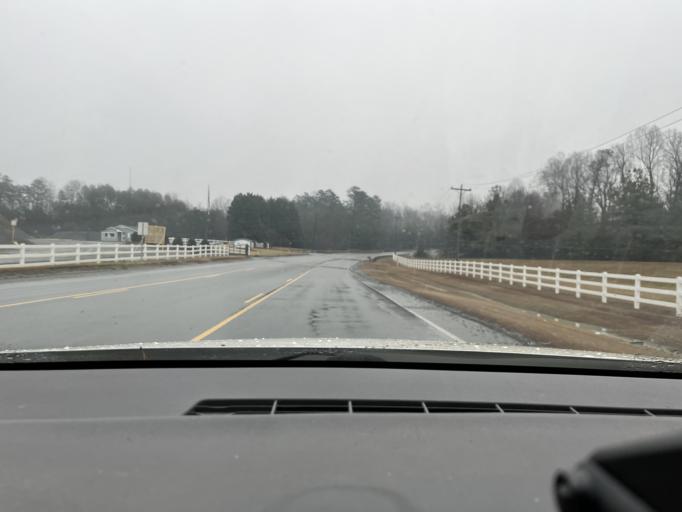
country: US
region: North Carolina
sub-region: Guilford County
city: Pleasant Garden
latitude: 36.0057
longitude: -79.7499
